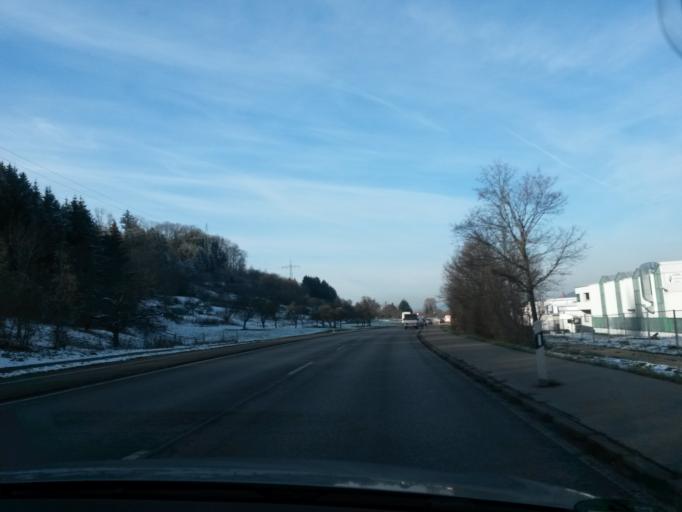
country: DE
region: Baden-Wuerttemberg
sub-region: Regierungsbezirk Stuttgart
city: Gingen an der Fils
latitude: 48.6484
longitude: 9.7856
